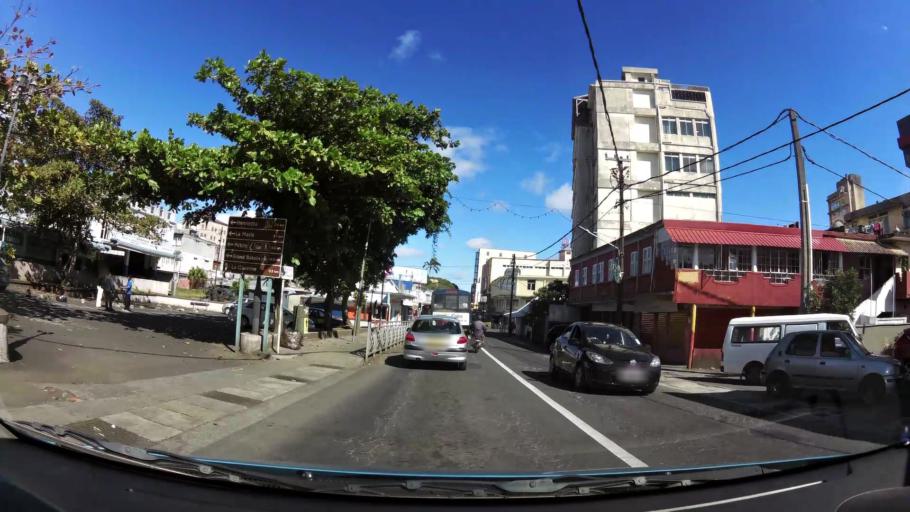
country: MU
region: Plaines Wilhems
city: Vacoas
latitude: -20.2986
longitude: 57.4934
